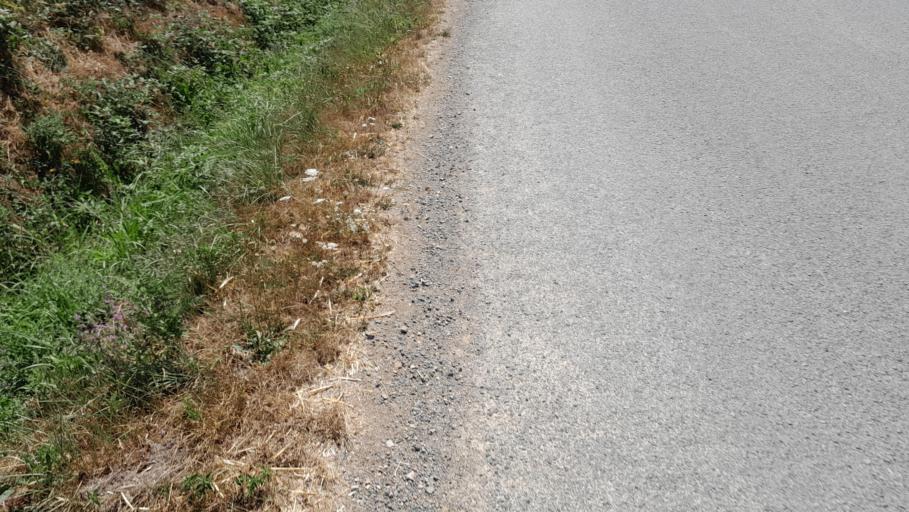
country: FR
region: Pays de la Loire
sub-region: Departement de la Mayenne
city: Ballots
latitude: 47.9609
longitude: -1.0409
